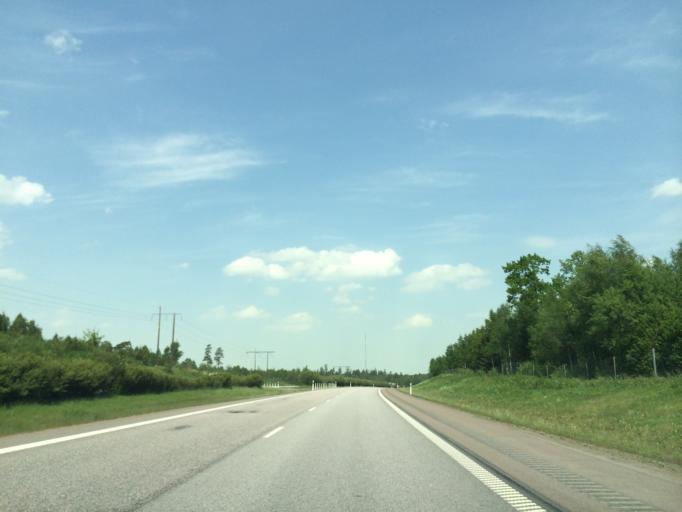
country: SE
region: OEstergoetland
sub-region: Vadstena Kommun
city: Herrestad
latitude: 58.2770
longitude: 14.8664
